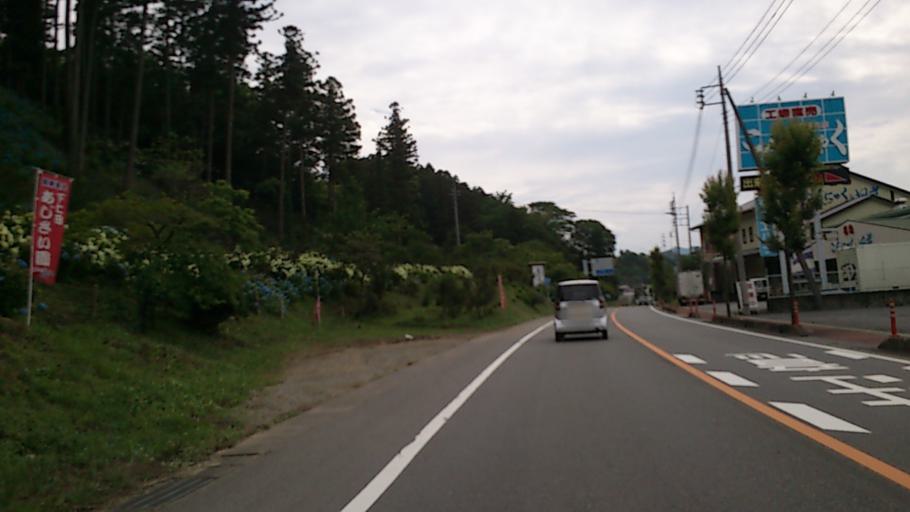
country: JP
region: Gunma
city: Tomioka
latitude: 36.2303
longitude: 138.8188
